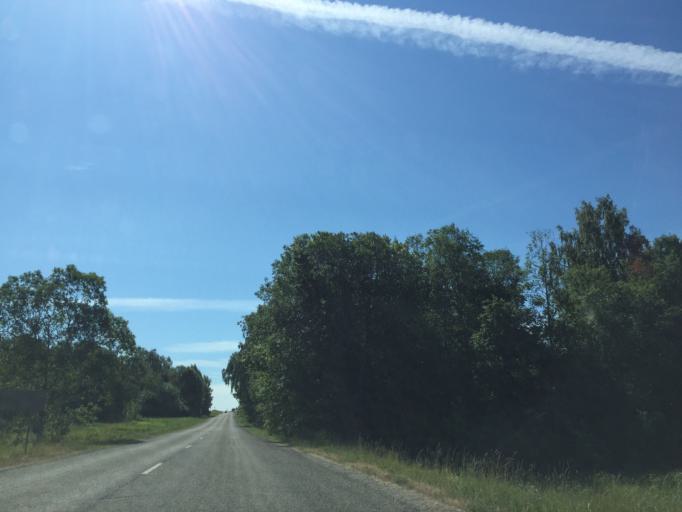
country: LV
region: Aizpute
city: Aizpute
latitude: 56.7087
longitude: 21.7683
